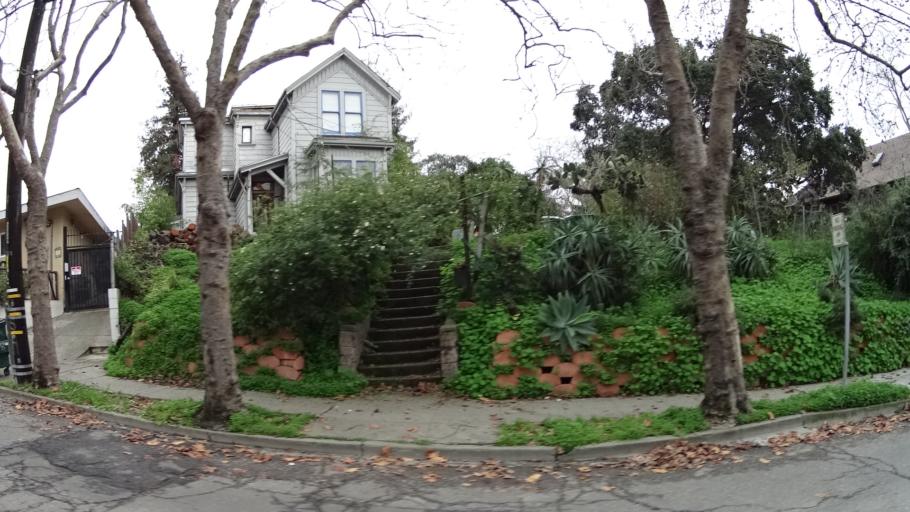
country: US
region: California
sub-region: Alameda County
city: Piedmont
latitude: 37.7997
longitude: -122.2350
